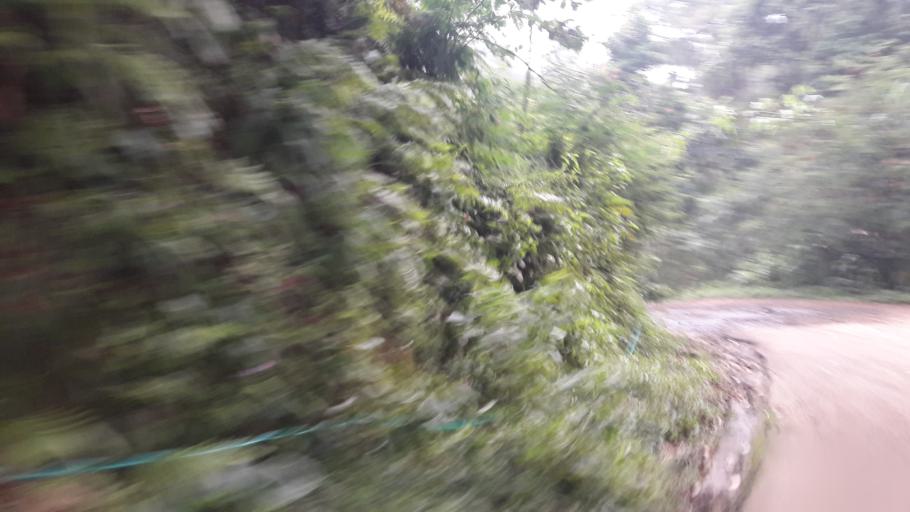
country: ID
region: West Java
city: Cipeundeuy
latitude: -6.6763
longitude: 106.5169
